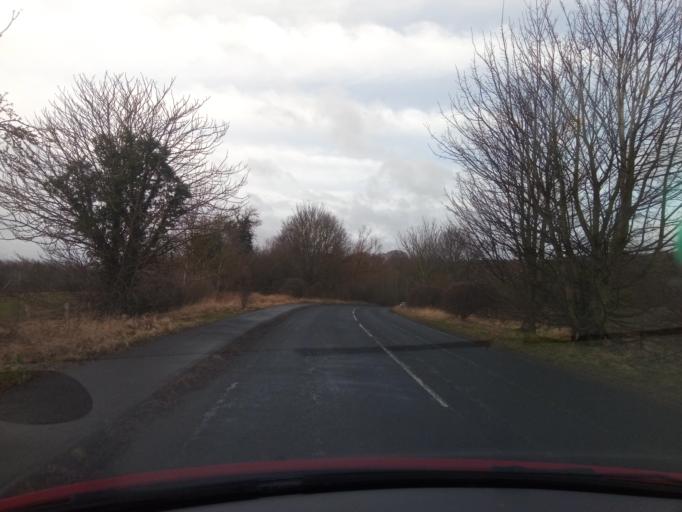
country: GB
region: England
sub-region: Northumberland
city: Corbridge
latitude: 54.9802
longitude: -2.0305
